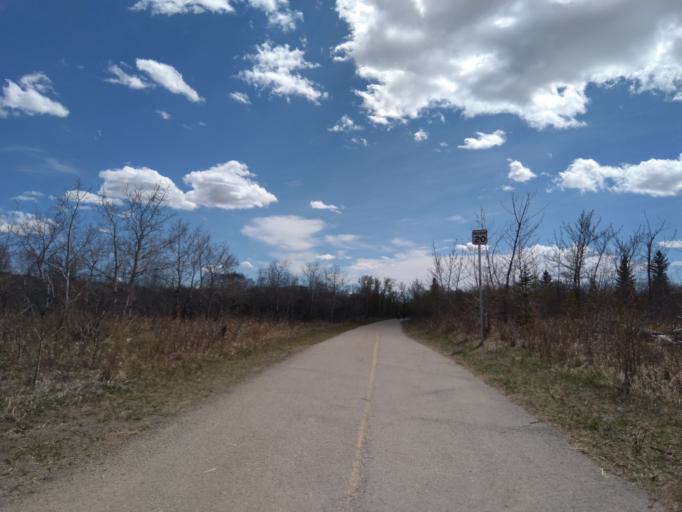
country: CA
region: Alberta
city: Calgary
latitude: 51.0922
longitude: -114.1821
